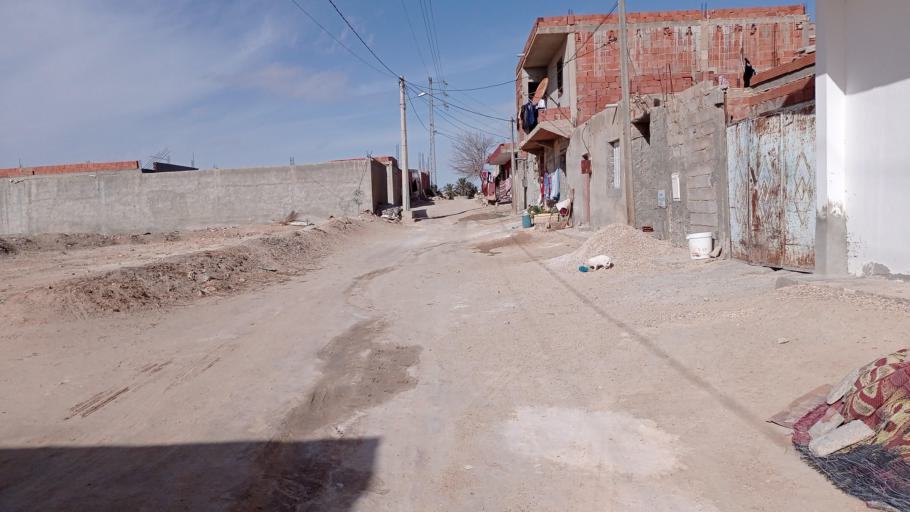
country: TN
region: Qabis
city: Gabes
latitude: 33.8341
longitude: 10.1098
